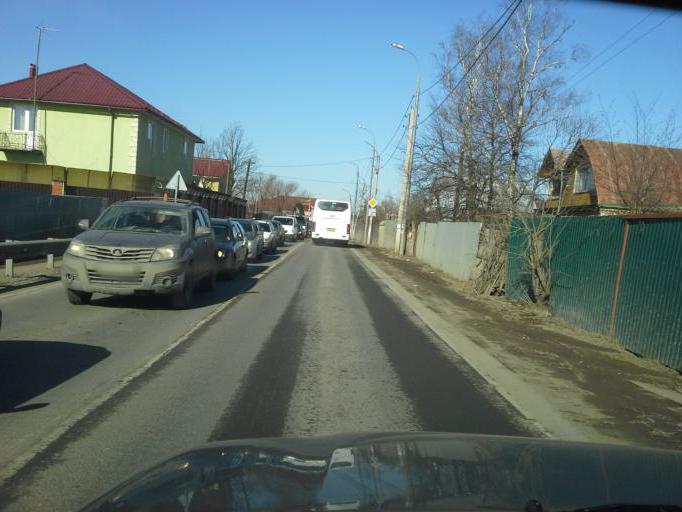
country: RU
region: Moskovskaya
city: Lesnoy Gorodok
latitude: 55.6594
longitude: 37.1860
